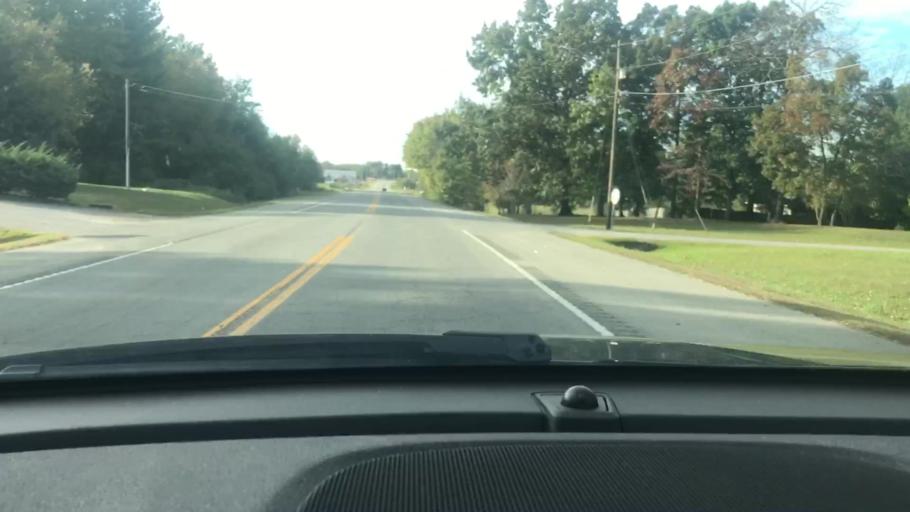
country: US
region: Tennessee
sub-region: Dickson County
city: White Bluff
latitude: 36.1284
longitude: -87.2292
